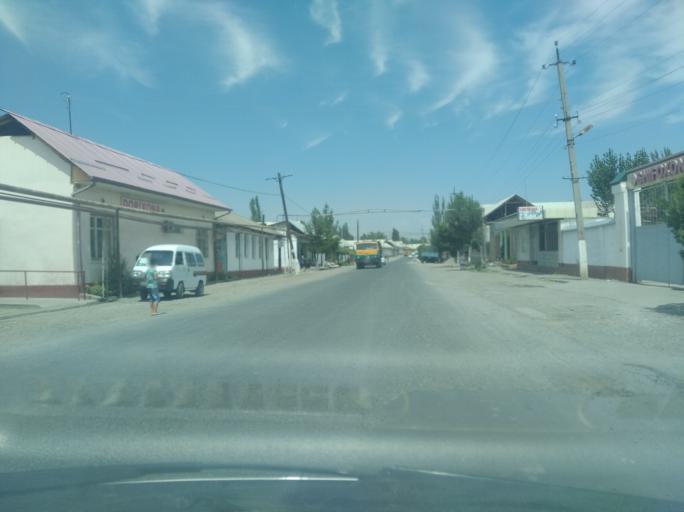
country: KG
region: Osh
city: Aravan
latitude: 40.6217
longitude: 72.4517
